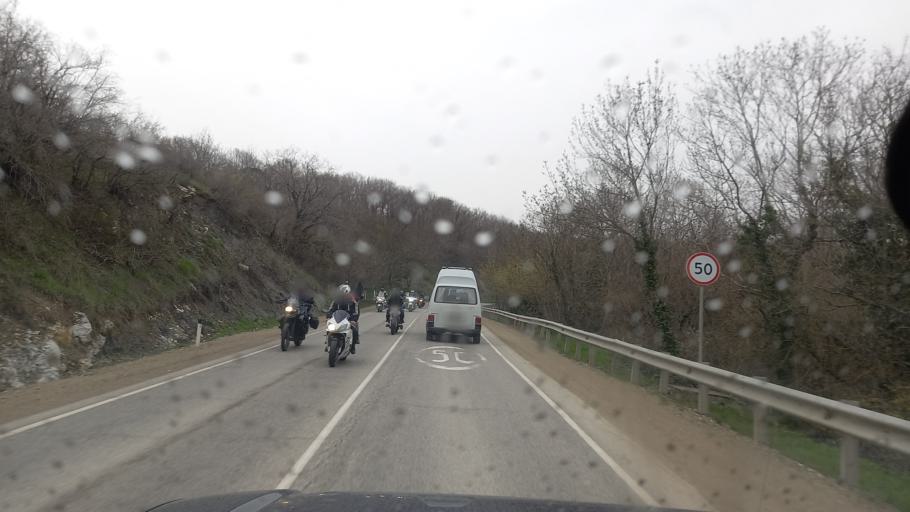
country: RU
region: Krasnodarskiy
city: Gayduk
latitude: 44.7386
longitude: 37.6782
